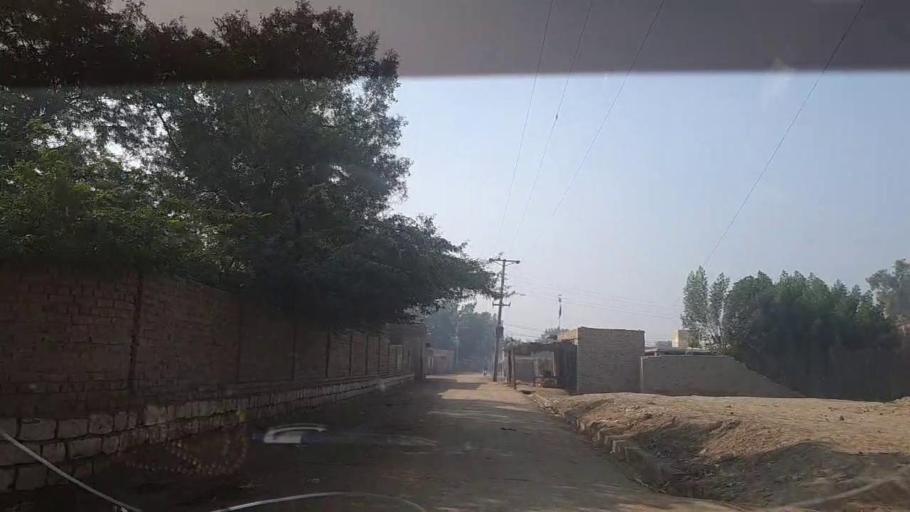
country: PK
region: Sindh
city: Khairpur
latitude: 27.4716
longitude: 68.7112
